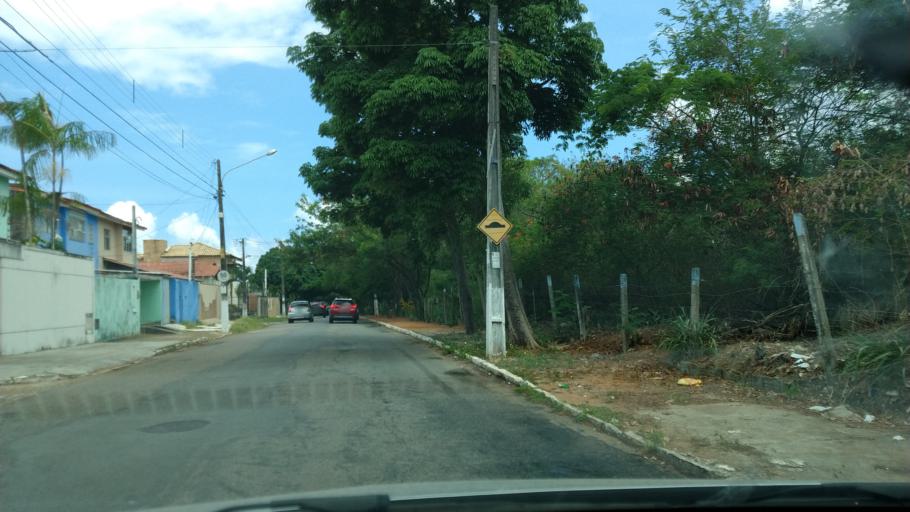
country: BR
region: Rio Grande do Norte
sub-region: Natal
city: Natal
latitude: -5.8513
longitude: -35.1988
